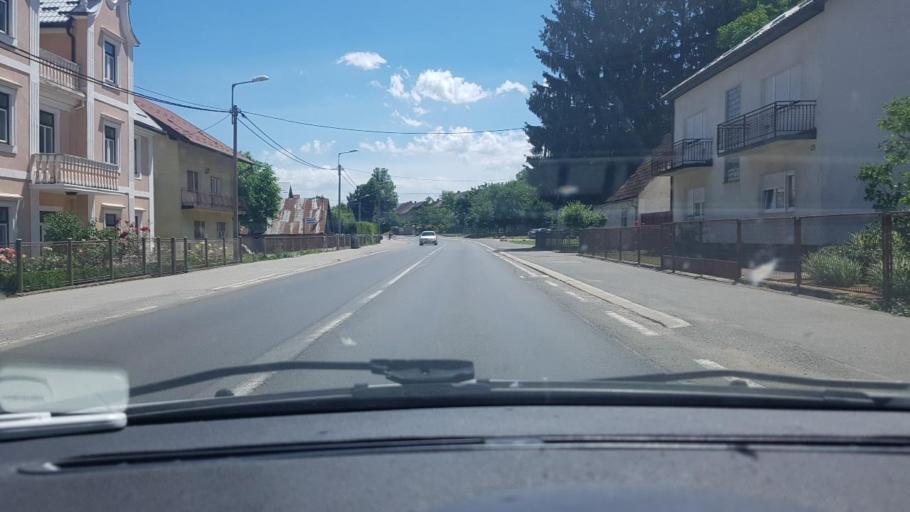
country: HR
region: Licko-Senjska
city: Otocac
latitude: 44.8690
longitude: 15.2444
